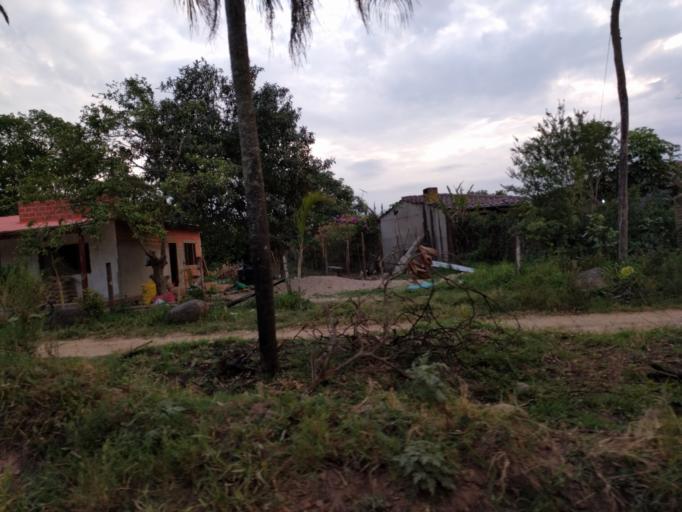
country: BO
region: Santa Cruz
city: Santa Rita
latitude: -17.9443
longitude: -63.3588
